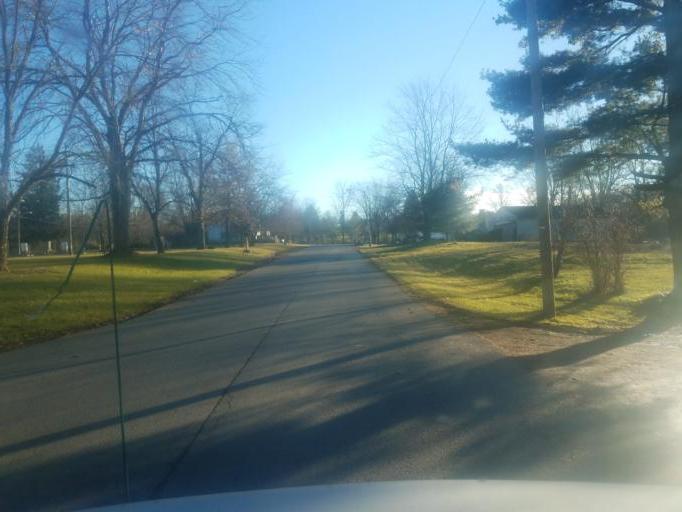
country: US
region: Ohio
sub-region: Richland County
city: Mansfield
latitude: 40.7893
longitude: -82.5389
